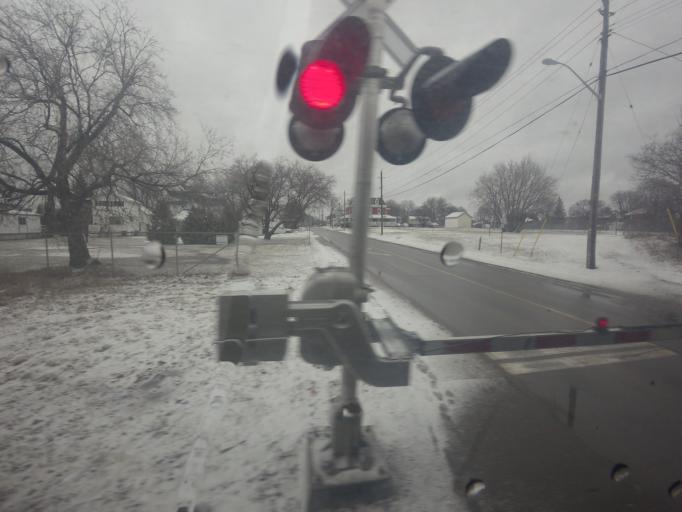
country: CA
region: Ontario
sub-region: Lanark County
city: Smiths Falls
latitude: 44.9015
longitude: -76.0127
